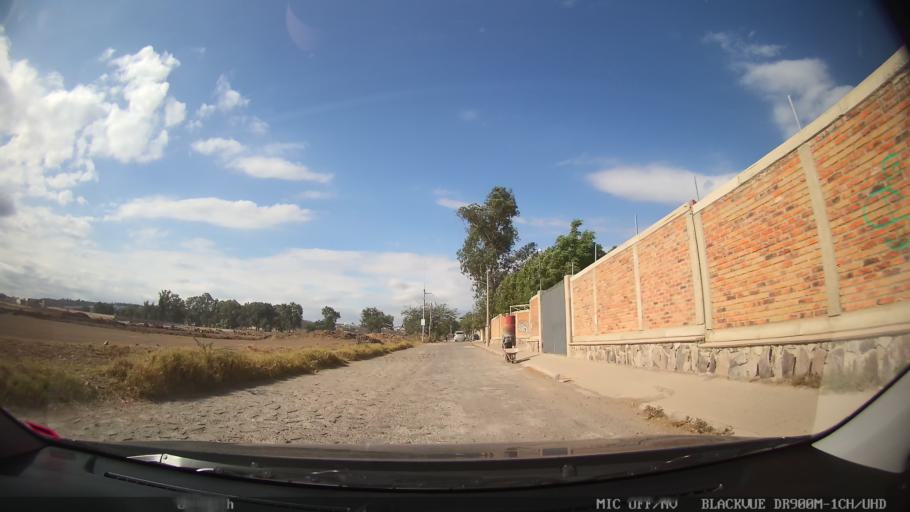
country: MX
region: Jalisco
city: Tonala
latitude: 20.6525
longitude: -103.2472
